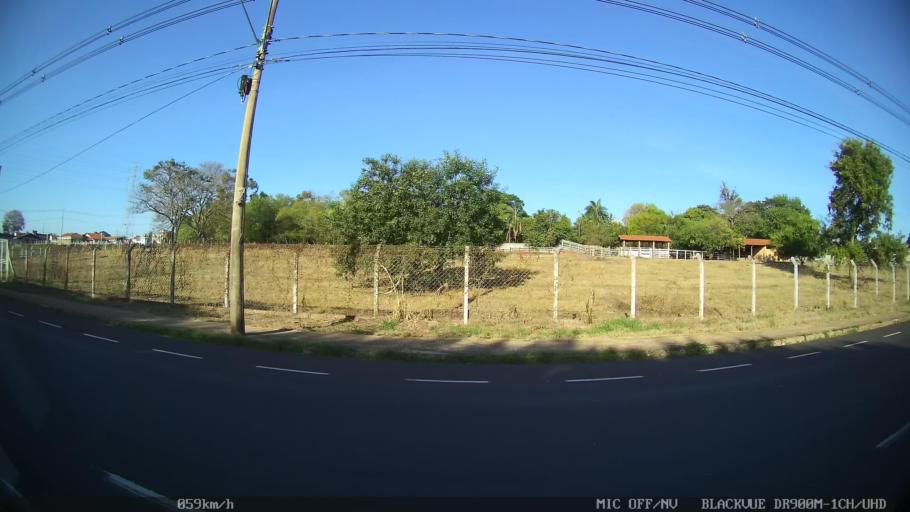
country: BR
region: Sao Paulo
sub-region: Sao Jose Do Rio Preto
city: Sao Jose do Rio Preto
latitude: -20.8443
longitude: -49.4110
